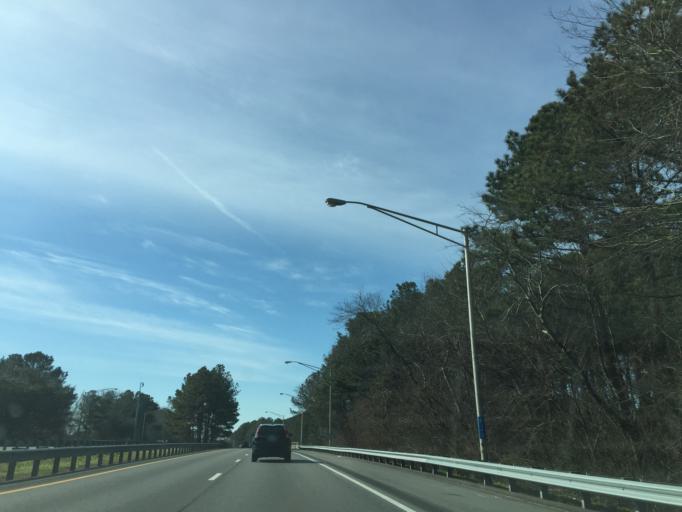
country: US
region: Virginia
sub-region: City of Norfolk
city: Norfolk
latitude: 36.9297
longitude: -76.2681
